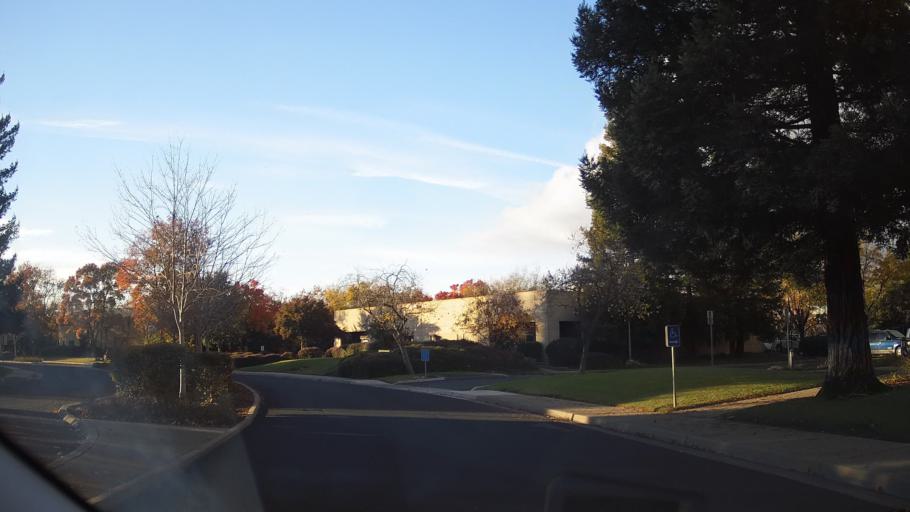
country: US
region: California
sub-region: Yolo County
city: West Sacramento
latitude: 38.5731
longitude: -121.5526
